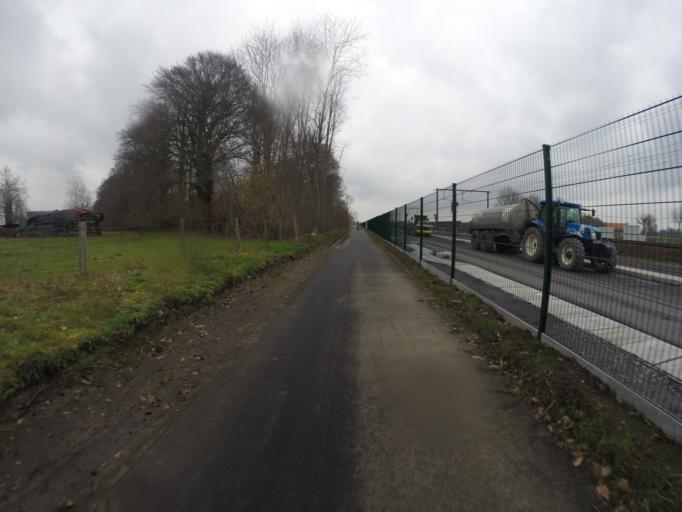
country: BE
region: Flanders
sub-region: Provincie Oost-Vlaanderen
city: Aalter
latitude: 51.0984
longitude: 3.4202
